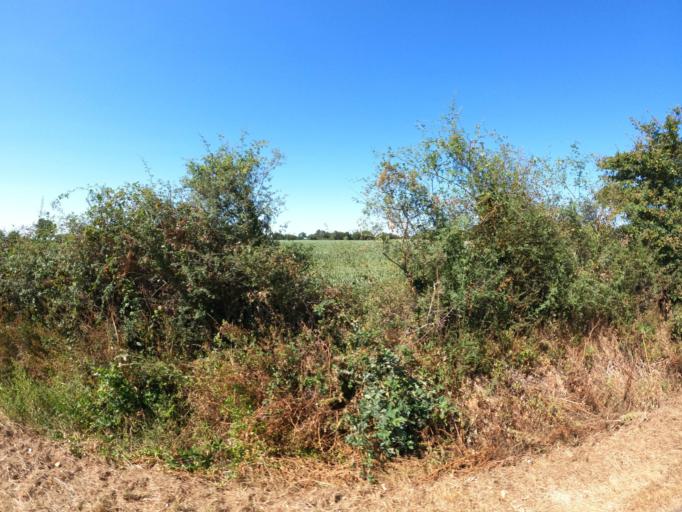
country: FR
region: Pays de la Loire
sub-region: Departement de la Vendee
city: La Gaubretiere
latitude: 46.9696
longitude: -1.0771
